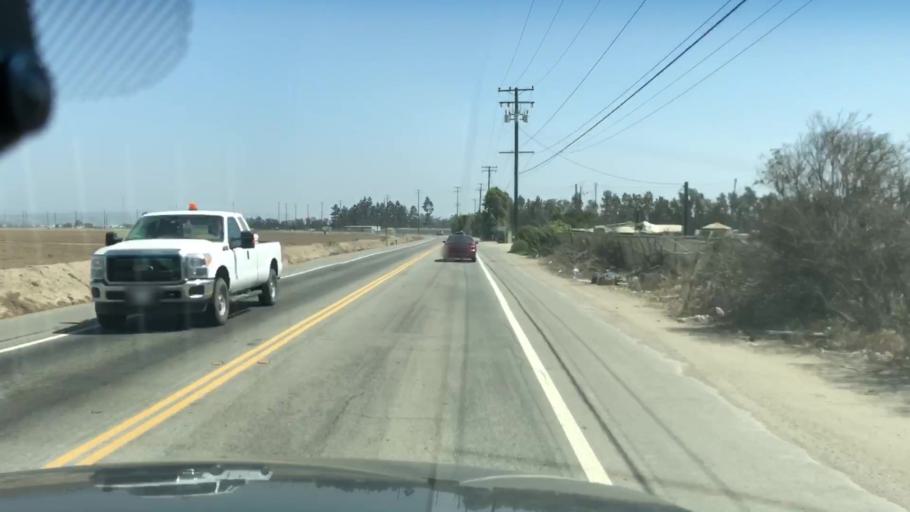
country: US
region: California
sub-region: Ventura County
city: Oxnard
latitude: 34.1733
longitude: -119.1279
